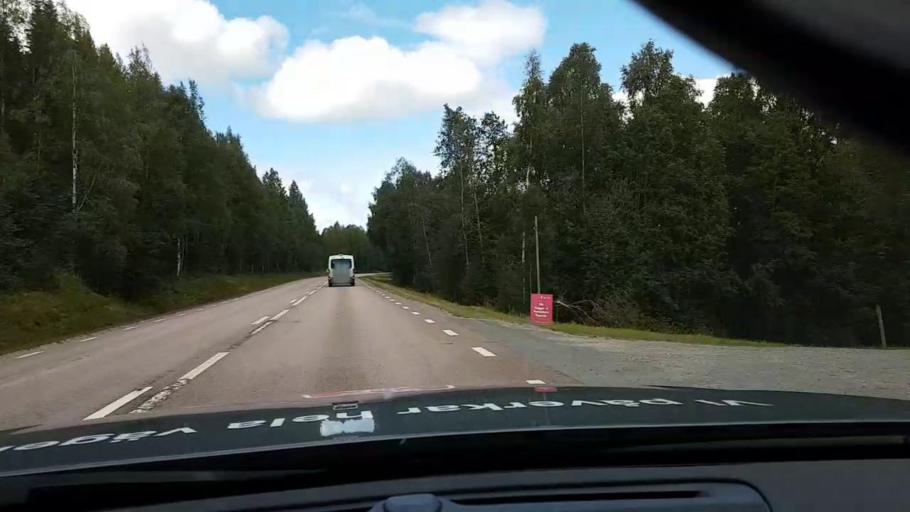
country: SE
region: Vaesternorrland
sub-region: OErnskoeldsviks Kommun
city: Bjasta
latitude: 63.3645
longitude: 18.4530
